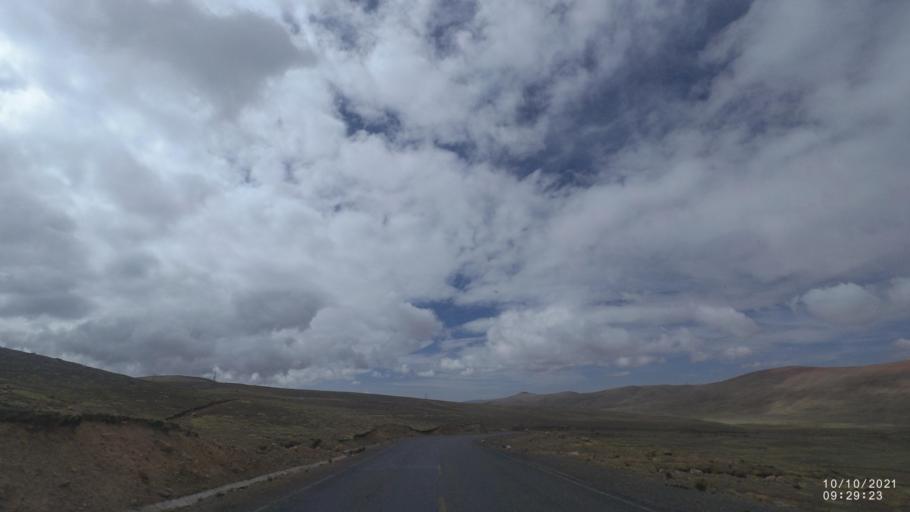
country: BO
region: La Paz
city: Quime
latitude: -17.1134
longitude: -67.3272
